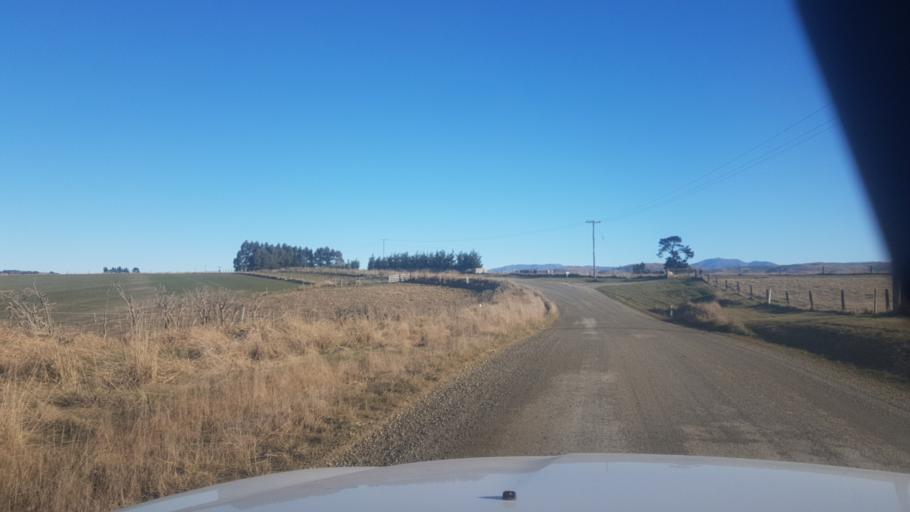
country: NZ
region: Canterbury
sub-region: Timaru District
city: Pleasant Point
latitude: -44.3467
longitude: 171.0749
